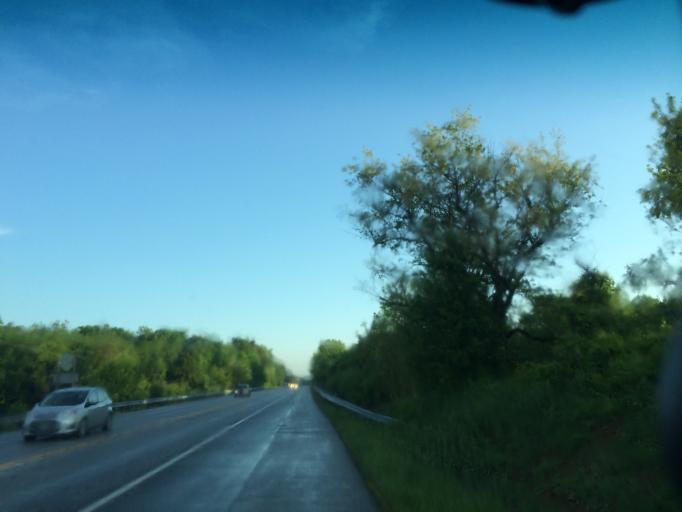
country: US
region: Maryland
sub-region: Carroll County
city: Eldersburg
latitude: 39.4596
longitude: -77.0021
